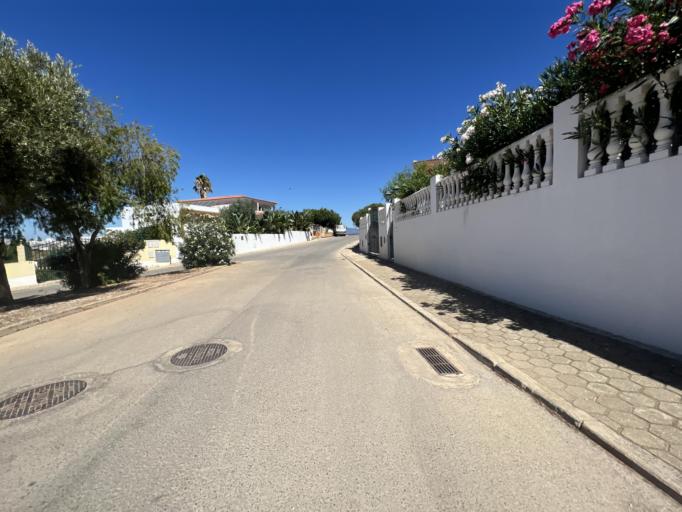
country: PT
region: Faro
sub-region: Portimao
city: Portimao
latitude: 37.1304
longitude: -8.5196
